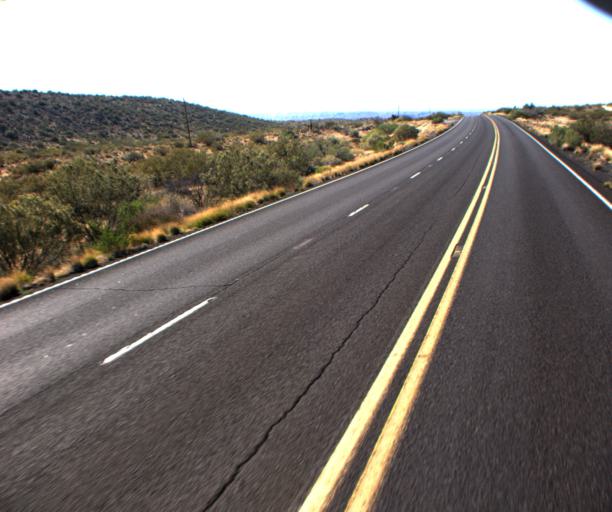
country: US
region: Arizona
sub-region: Mohave County
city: Kingman
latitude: 34.9429
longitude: -113.6659
